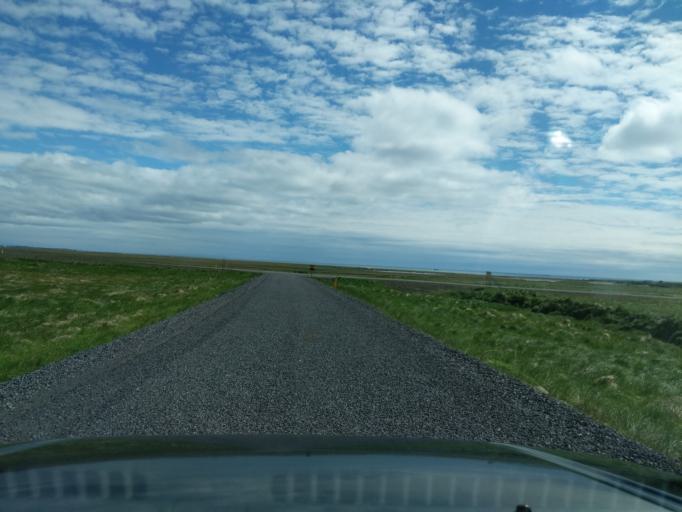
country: IS
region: West
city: Olafsvik
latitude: 64.8420
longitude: -23.3993
